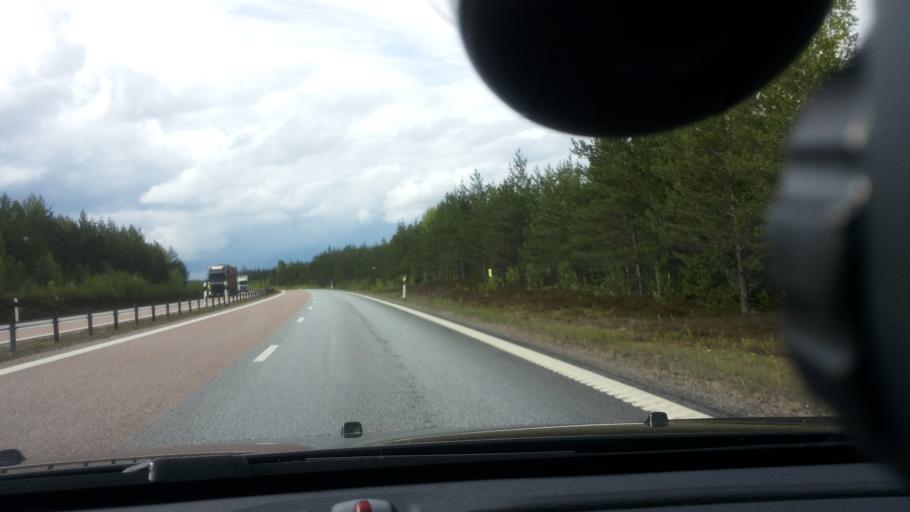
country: SE
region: Gaevleborg
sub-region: Soderhamns Kommun
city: Soderhamn
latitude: 61.4081
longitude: 16.9939
